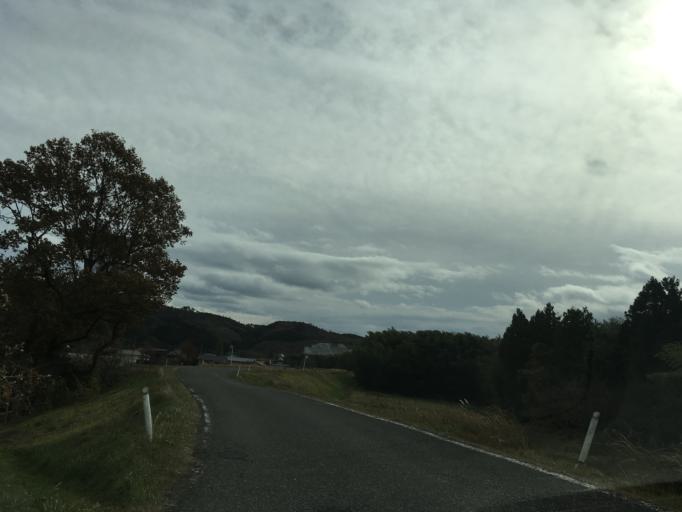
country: JP
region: Iwate
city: Ichinoseki
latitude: 38.7588
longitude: 141.2773
